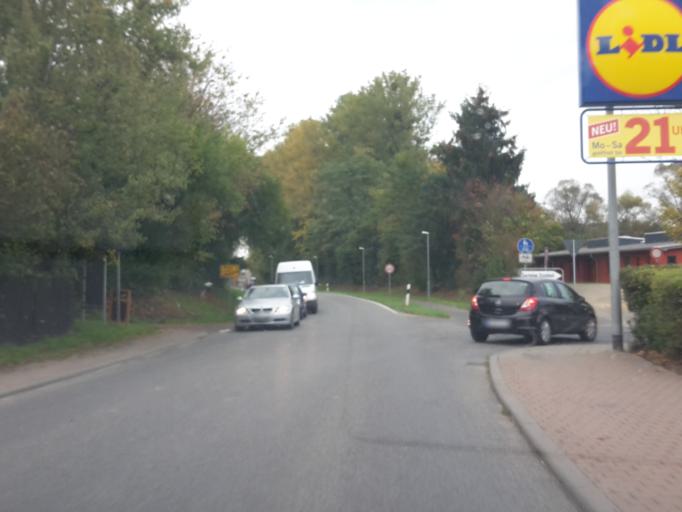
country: DE
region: Hesse
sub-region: Regierungsbezirk Darmstadt
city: Idstein
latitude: 50.2290
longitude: 8.2640
